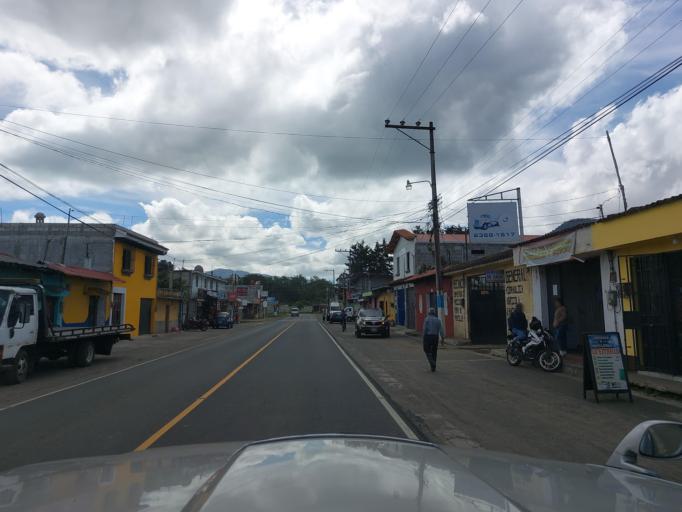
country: GT
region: Chimaltenango
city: Parramos
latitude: 14.6097
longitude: -90.7998
